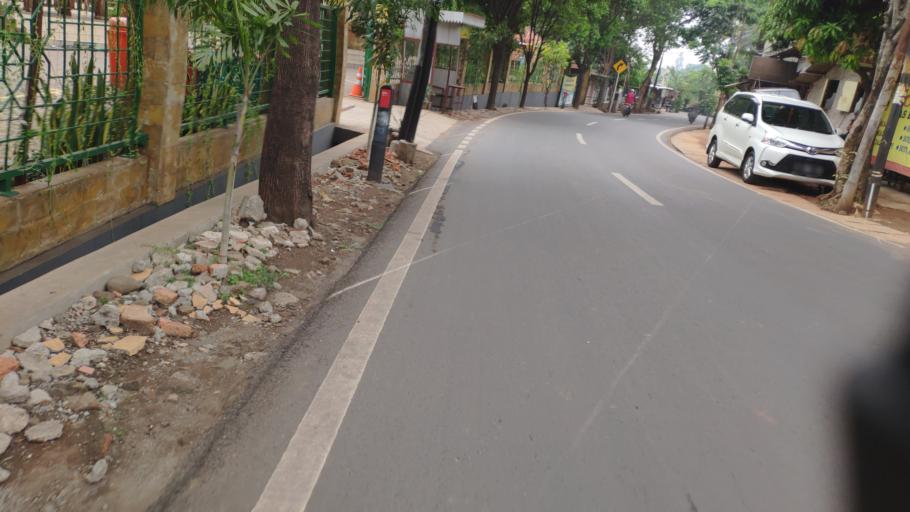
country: ID
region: West Java
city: Depok
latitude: -6.3464
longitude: 106.8208
